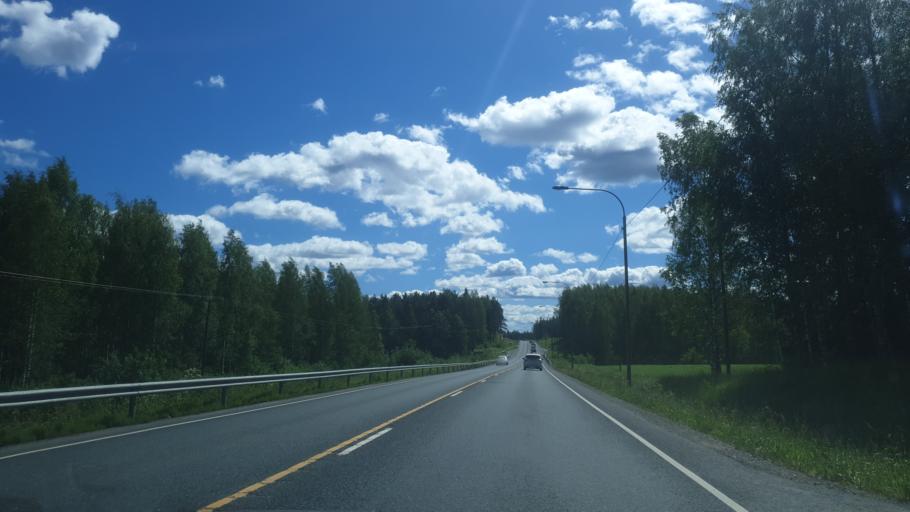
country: FI
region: Northern Savo
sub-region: Varkaus
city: Leppaevirta
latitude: 62.5322
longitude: 27.6551
